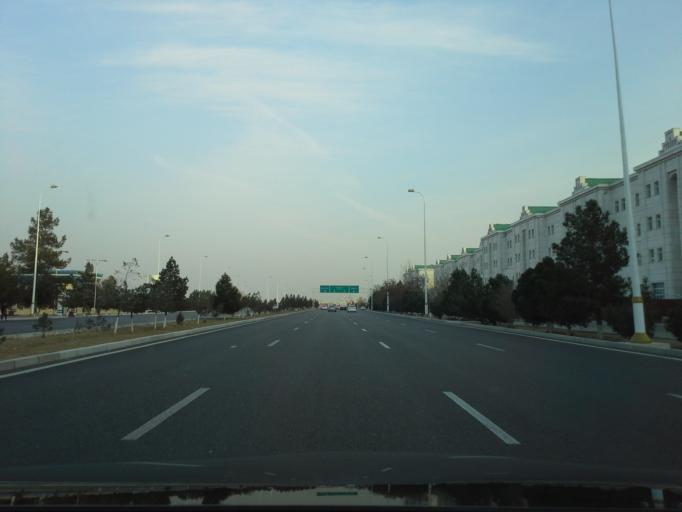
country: TM
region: Ahal
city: Ashgabat
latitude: 37.9881
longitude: 58.3233
